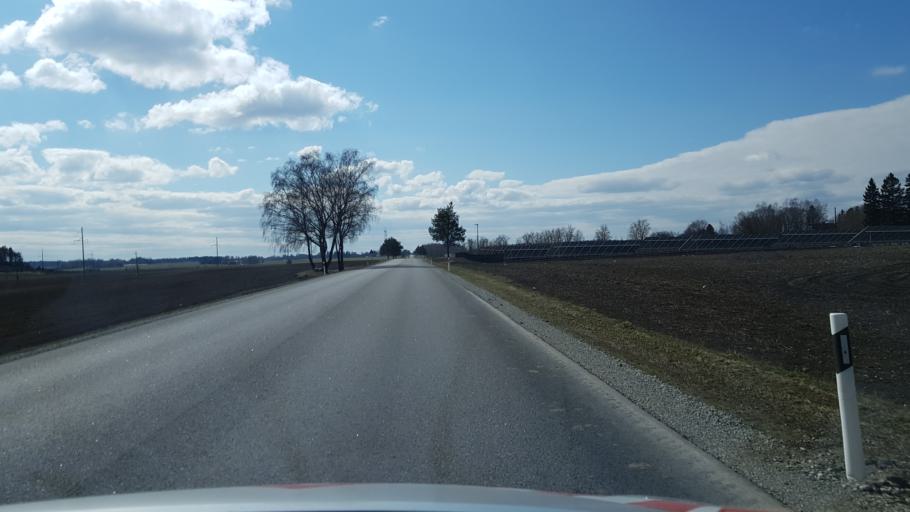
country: EE
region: Laeaene-Virumaa
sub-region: Rakvere linn
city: Rakvere
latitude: 59.3109
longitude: 26.3248
